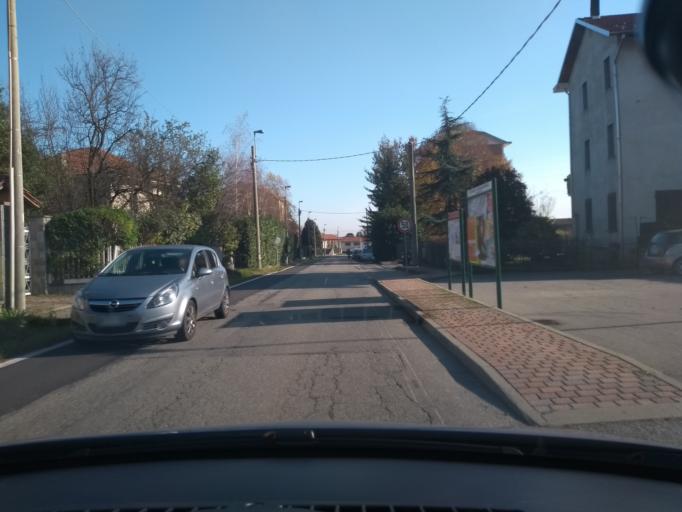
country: IT
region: Piedmont
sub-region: Provincia di Torino
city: Robassomero
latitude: 45.2034
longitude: 7.5622
